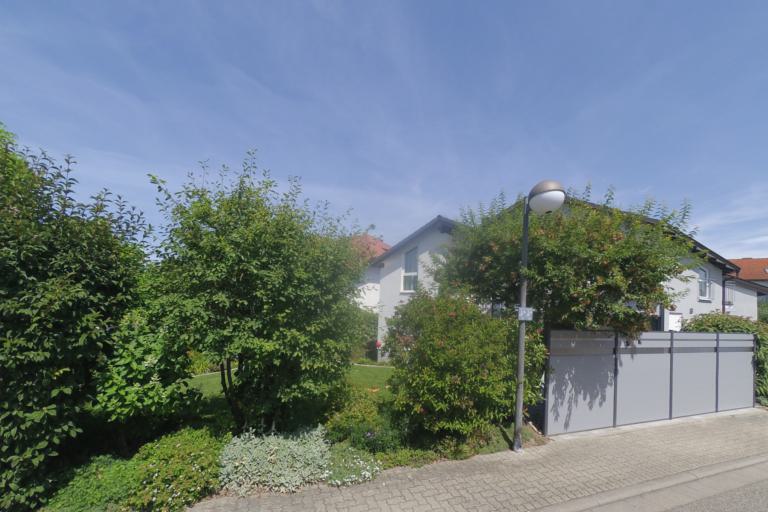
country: DE
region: Rheinland-Pfalz
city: Limburgerhof
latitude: 49.4261
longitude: 8.3803
